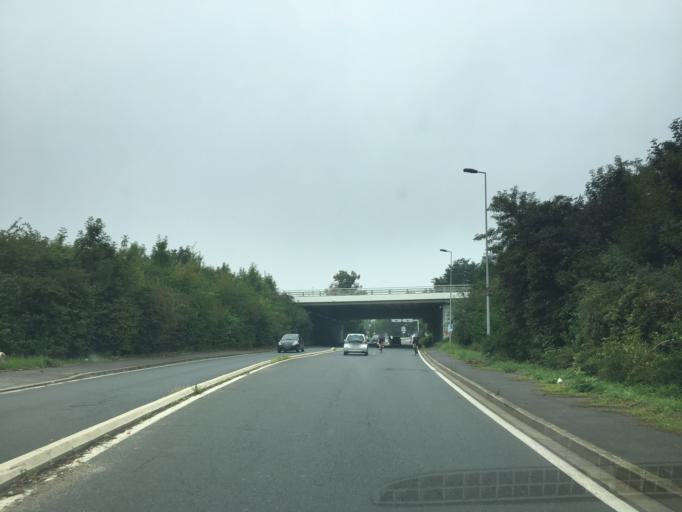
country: FR
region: Ile-de-France
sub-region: Departement de l'Essonne
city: Etiolles
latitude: 48.6253
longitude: 2.4751
